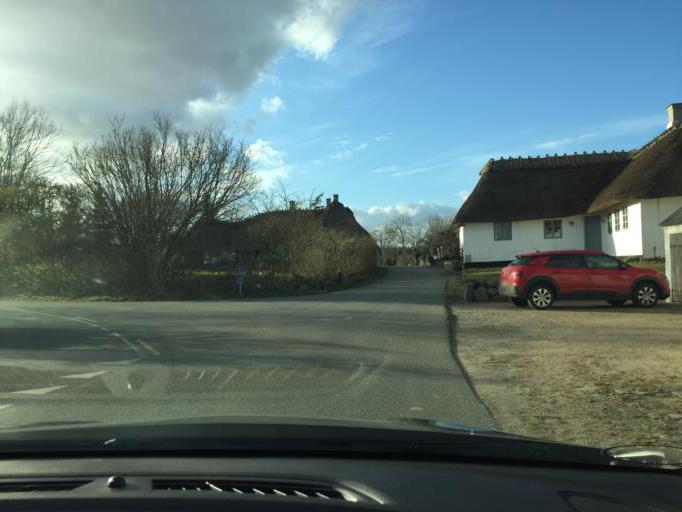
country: DK
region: South Denmark
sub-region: Kerteminde Kommune
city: Langeskov
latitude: 55.3433
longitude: 10.6083
